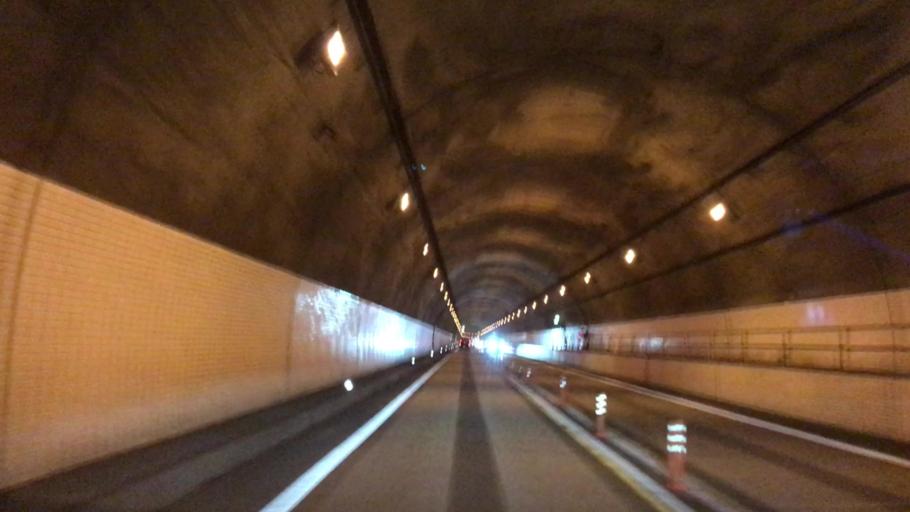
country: JP
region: Hokkaido
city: Chitose
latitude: 42.9134
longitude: 141.9402
